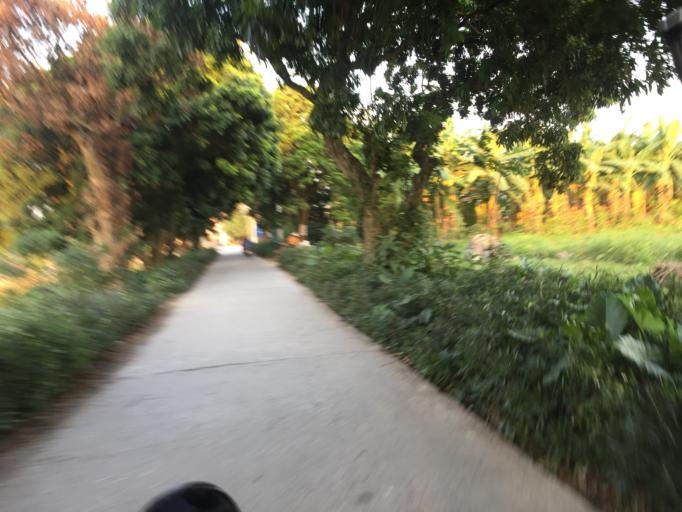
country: VN
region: Ha Noi
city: Chuc Son
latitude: 20.9076
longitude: 105.7269
